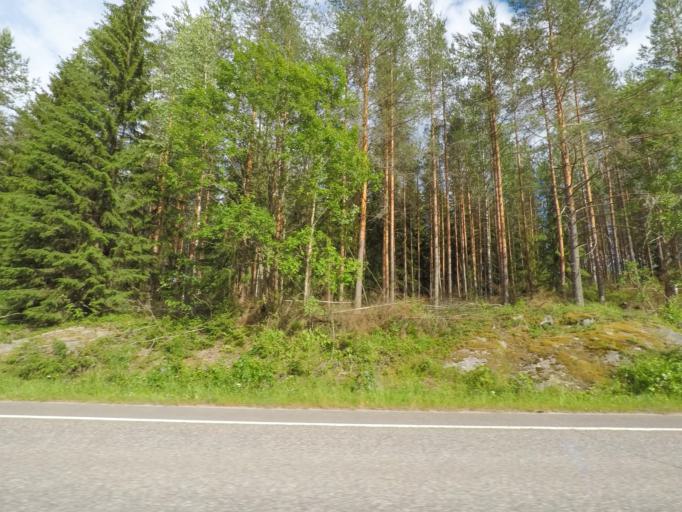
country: FI
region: Paijanne Tavastia
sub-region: Lahti
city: Hollola
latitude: 60.8158
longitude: 25.4826
